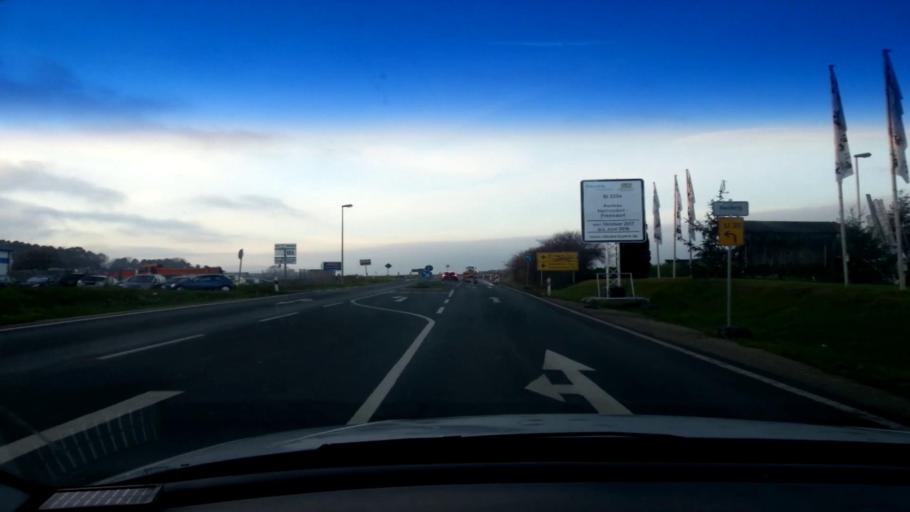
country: DE
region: Bavaria
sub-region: Upper Franconia
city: Frensdorf
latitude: 49.7943
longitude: 10.8836
